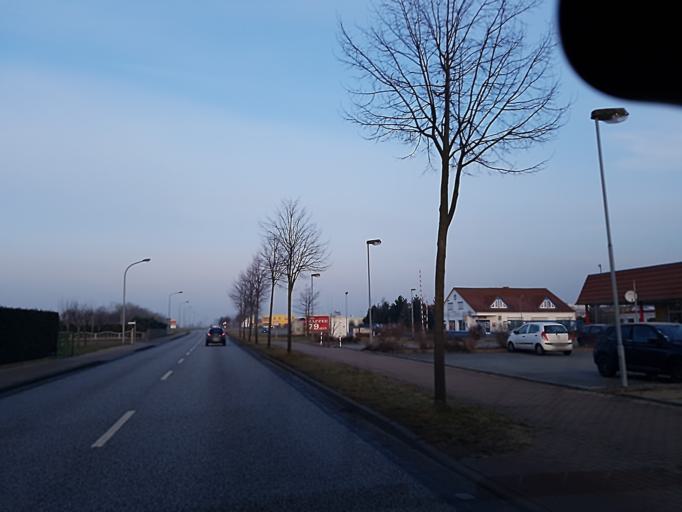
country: DE
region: Saxony-Anhalt
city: Elster
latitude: 51.8307
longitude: 12.8099
